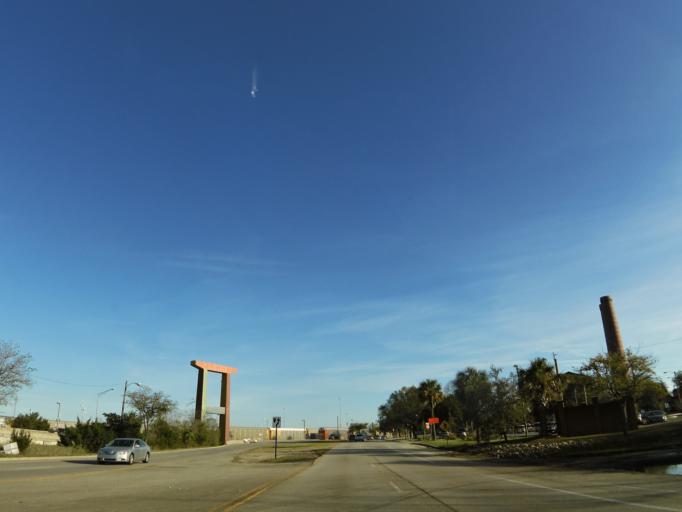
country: US
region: South Carolina
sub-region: Charleston County
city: Charleston
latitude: 32.8008
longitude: -79.9365
